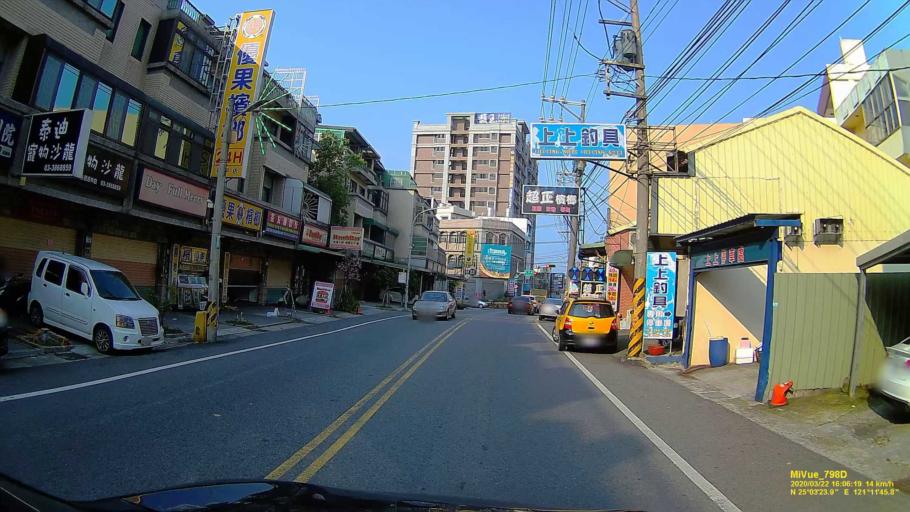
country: TW
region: Taiwan
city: Taoyuan City
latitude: 25.0567
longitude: 121.1961
